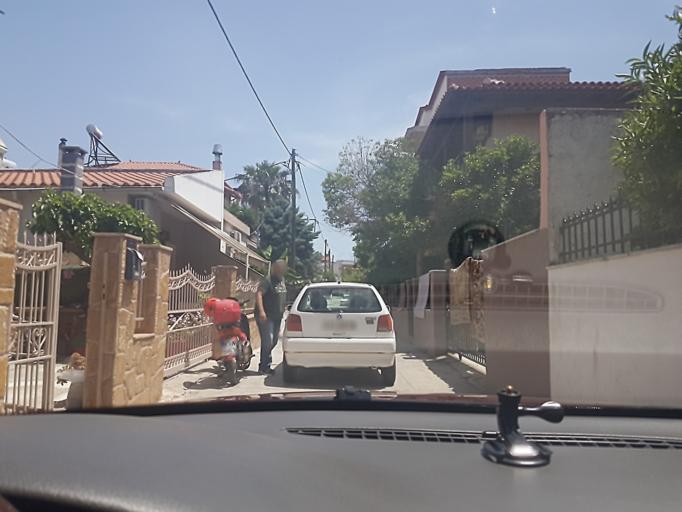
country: GR
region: Central Greece
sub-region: Nomos Evvoias
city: Vasilikon
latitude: 38.4247
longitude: 23.6694
